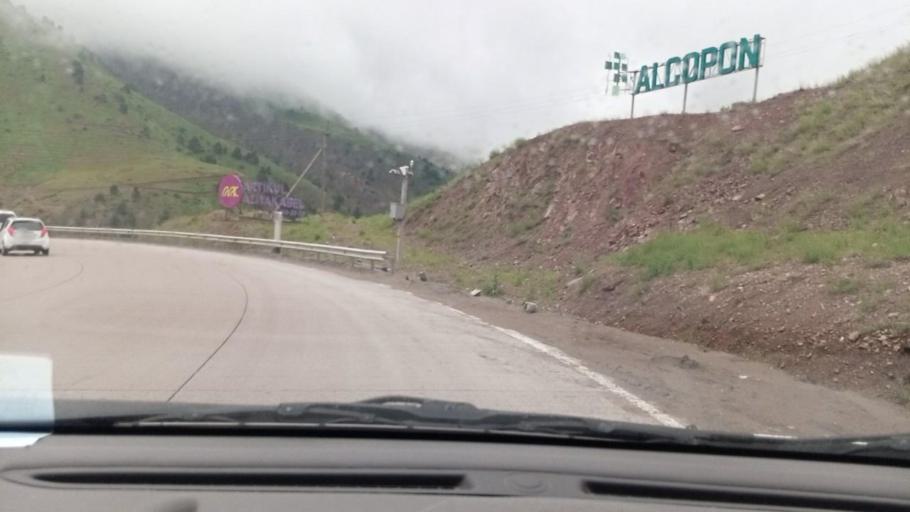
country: UZ
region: Toshkent
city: Angren
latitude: 41.1128
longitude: 70.5003
